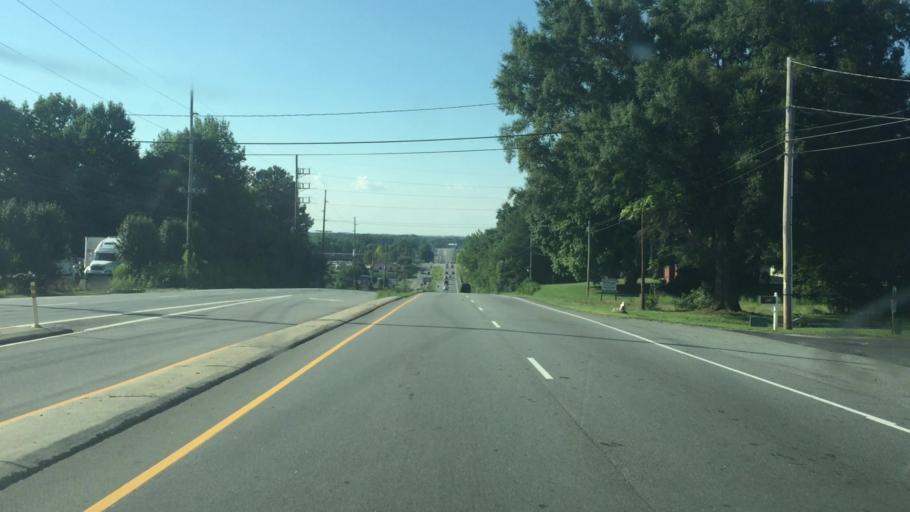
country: US
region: North Carolina
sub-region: Cabarrus County
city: Concord
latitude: 35.4038
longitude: -80.6094
